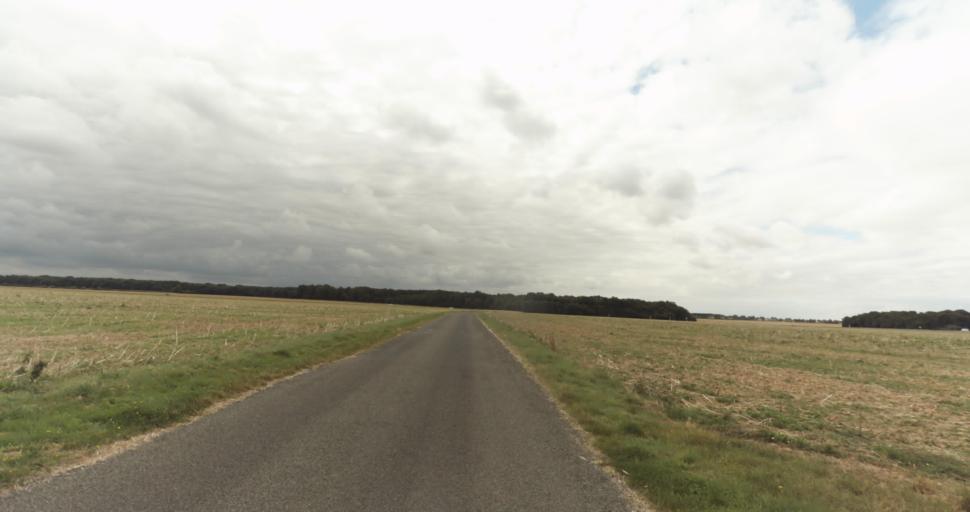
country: FR
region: Haute-Normandie
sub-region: Departement de l'Eure
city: Gravigny
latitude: 49.0173
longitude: 1.2639
